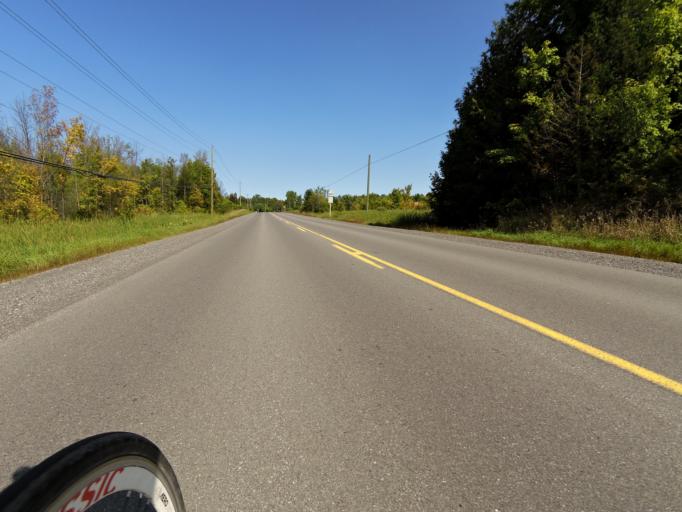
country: CA
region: Ontario
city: Arnprior
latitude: 45.4351
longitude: -76.1185
